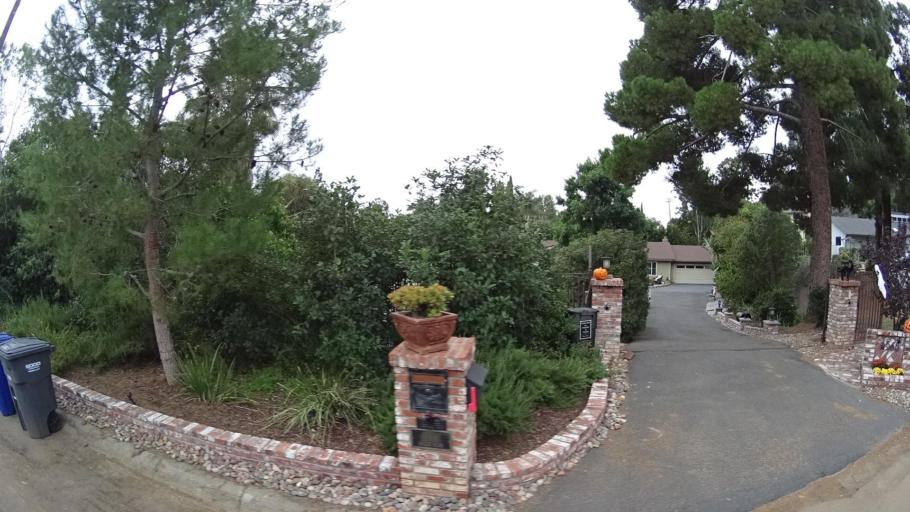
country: US
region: California
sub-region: San Diego County
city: Casa de Oro-Mount Helix
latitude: 32.7621
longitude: -116.9751
